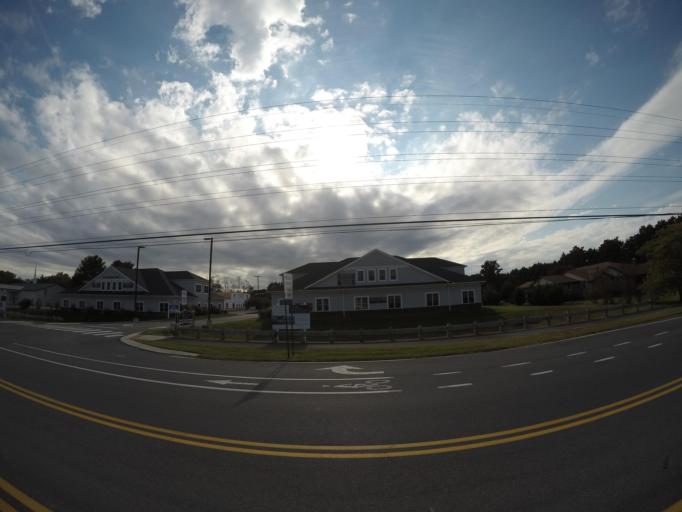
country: US
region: Delaware
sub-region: Sussex County
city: Lewes
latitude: 38.7284
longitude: -75.1476
